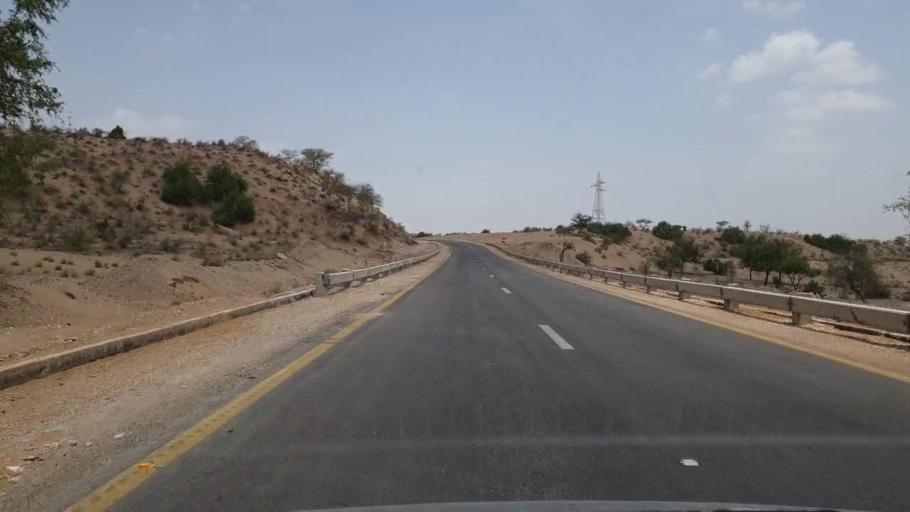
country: PK
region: Sindh
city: Mithi
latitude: 24.7951
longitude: 69.7461
